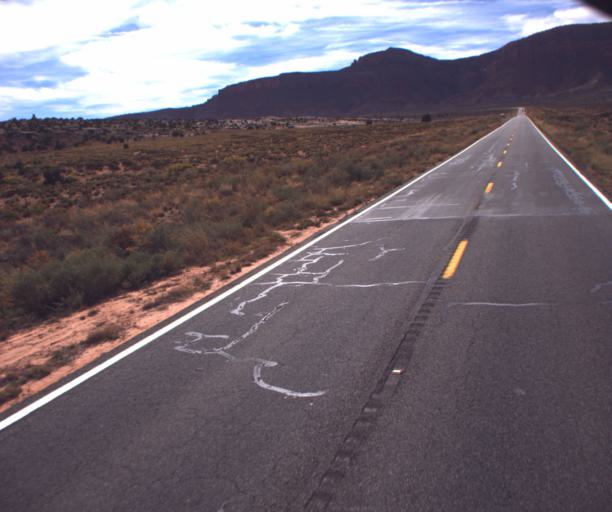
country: US
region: Arizona
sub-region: Navajo County
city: Kayenta
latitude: 36.8639
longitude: -110.2645
